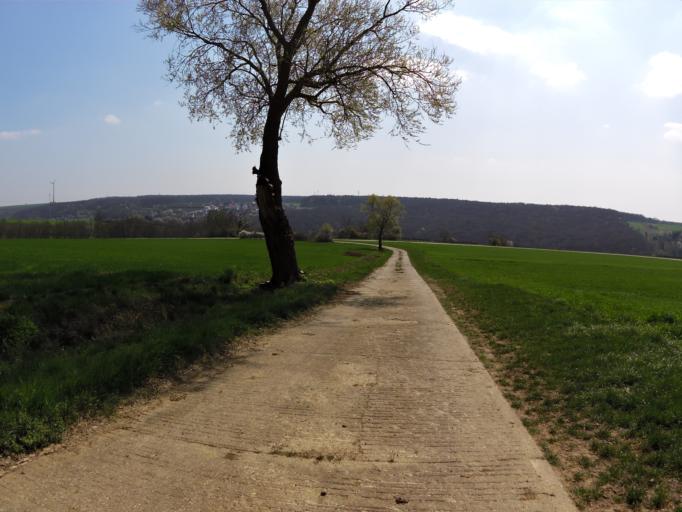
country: DE
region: Bavaria
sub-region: Regierungsbezirk Unterfranken
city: Theilheim
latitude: 49.7584
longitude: 10.0131
